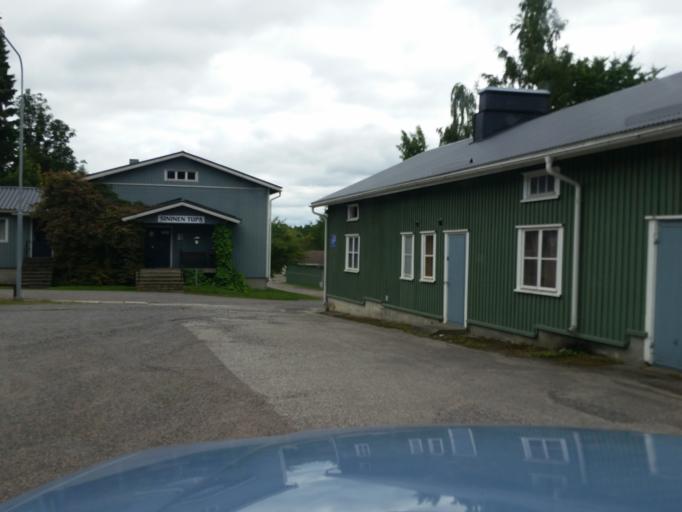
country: FI
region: Varsinais-Suomi
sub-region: Turku
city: Turku
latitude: 60.4306
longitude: 22.3009
